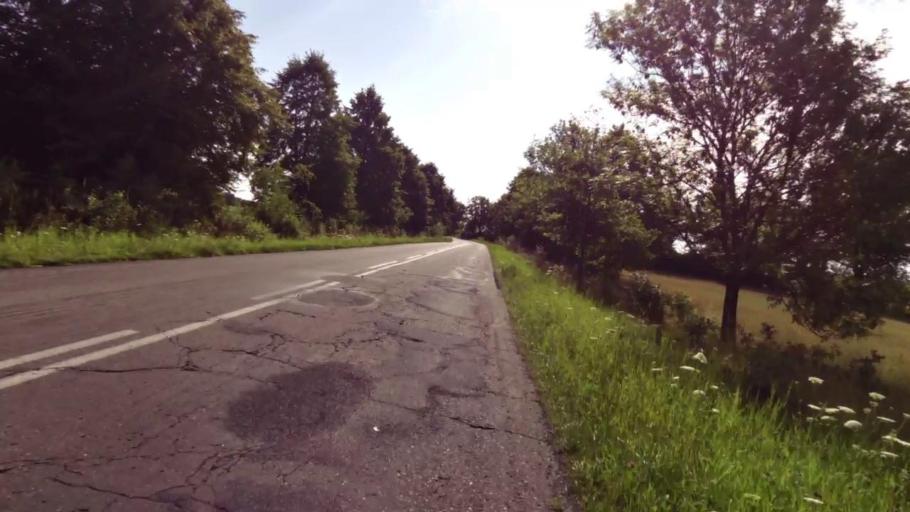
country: PL
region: West Pomeranian Voivodeship
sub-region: Powiat stargardzki
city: Marianowo
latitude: 53.3645
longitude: 15.3190
